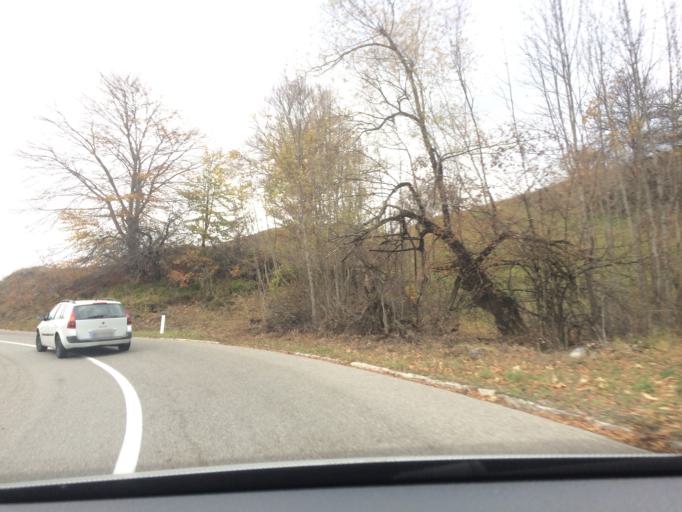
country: ME
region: Opstina Savnik
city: Savnik
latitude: 42.9456
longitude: 19.0772
